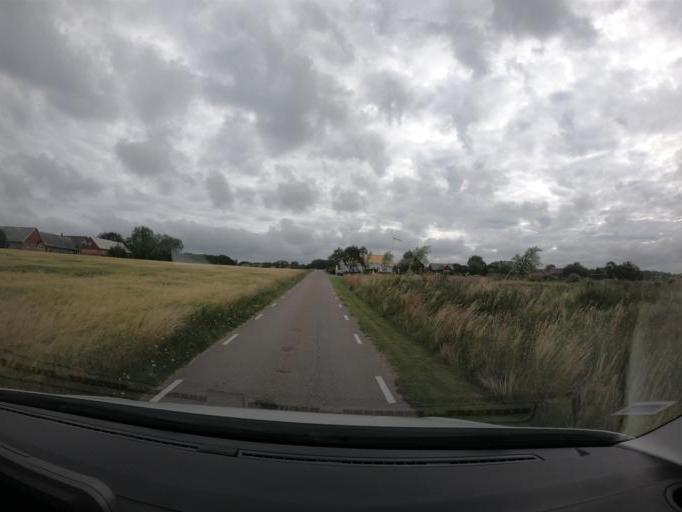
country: SE
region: Skane
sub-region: Bastads Kommun
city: Forslov
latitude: 56.3323
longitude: 12.8158
